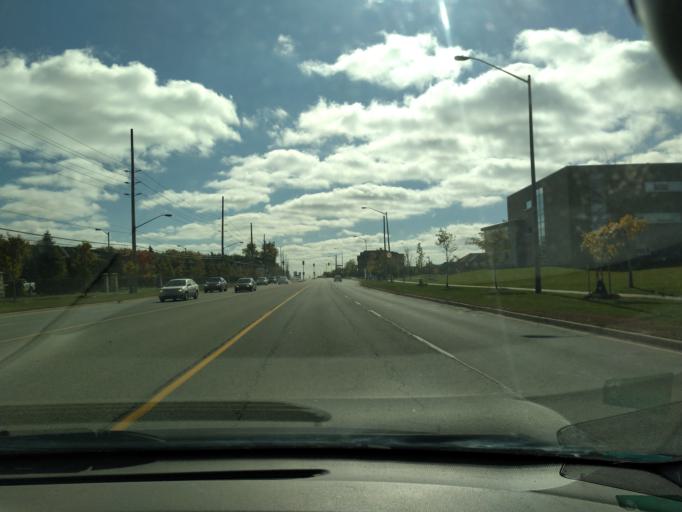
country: CA
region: Ontario
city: Vaughan
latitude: 43.8361
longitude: -79.5587
